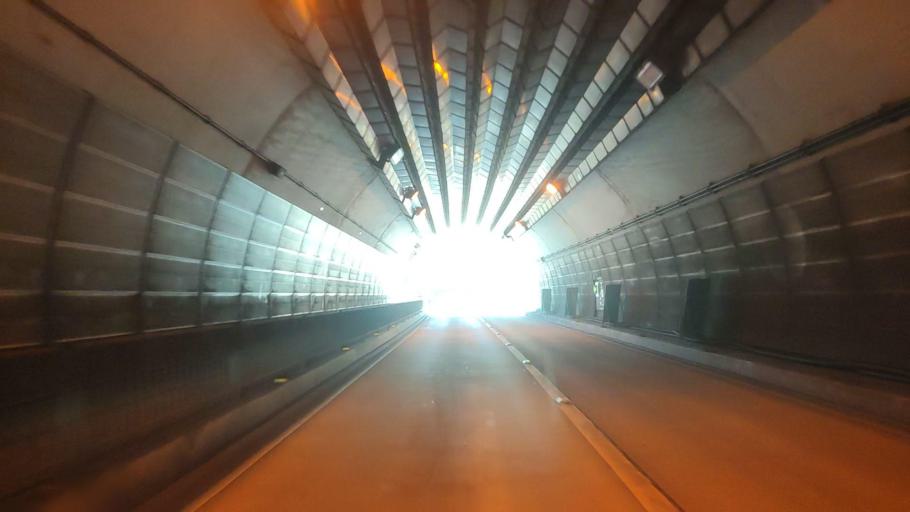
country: JP
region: Nara
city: Yoshino-cho
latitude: 34.3337
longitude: 135.9575
